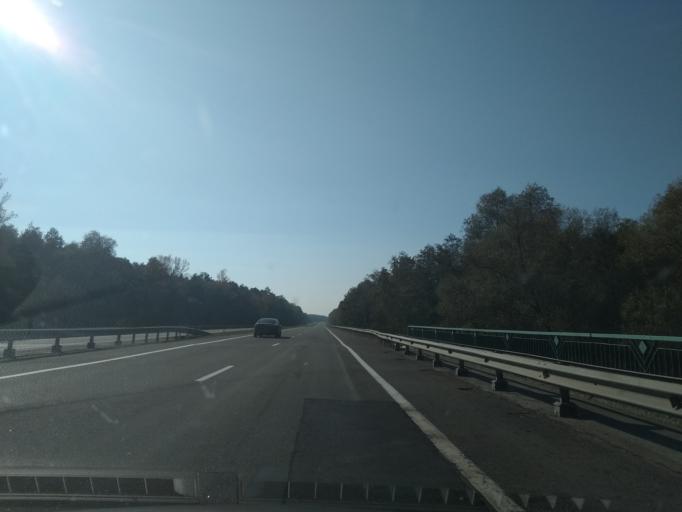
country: BY
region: Brest
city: Horad Kobryn
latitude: 52.2800
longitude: 24.5520
